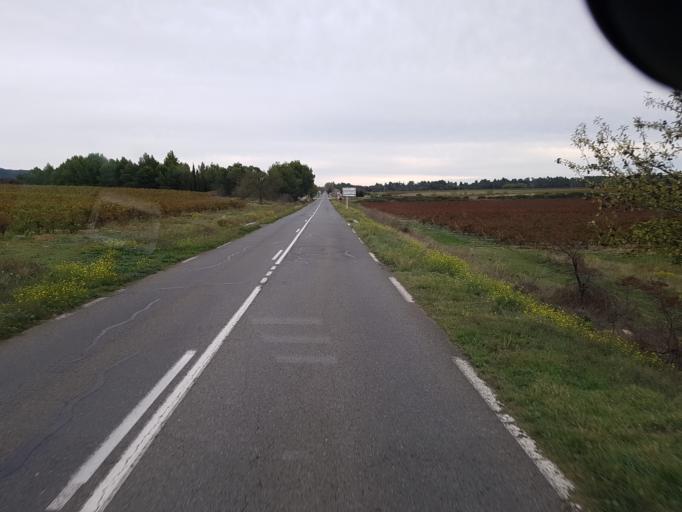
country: FR
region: Languedoc-Roussillon
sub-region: Departement de l'Aude
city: Caunes-Minervois
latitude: 43.3088
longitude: 2.4881
